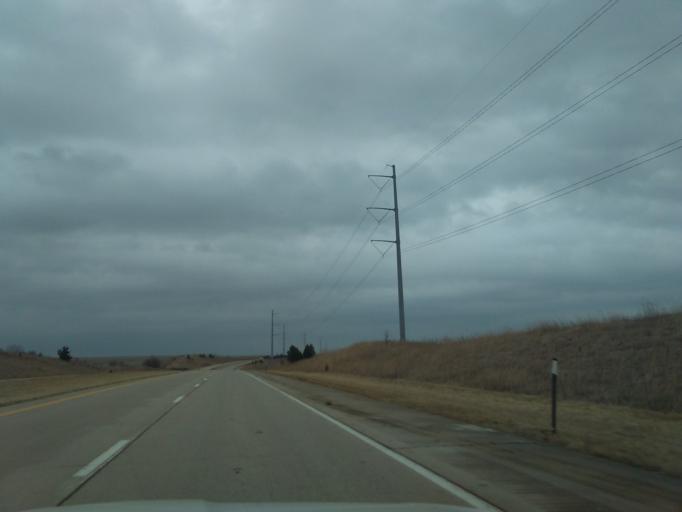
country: US
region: Nebraska
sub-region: Otoe County
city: Syracuse
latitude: 40.6738
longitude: -96.0845
